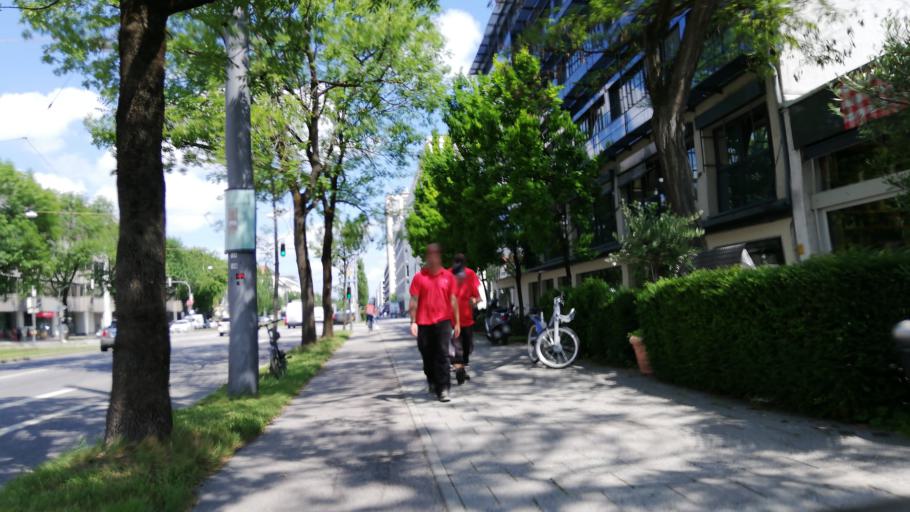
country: DE
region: Bavaria
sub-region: Upper Bavaria
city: Munich
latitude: 48.1690
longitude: 11.5864
